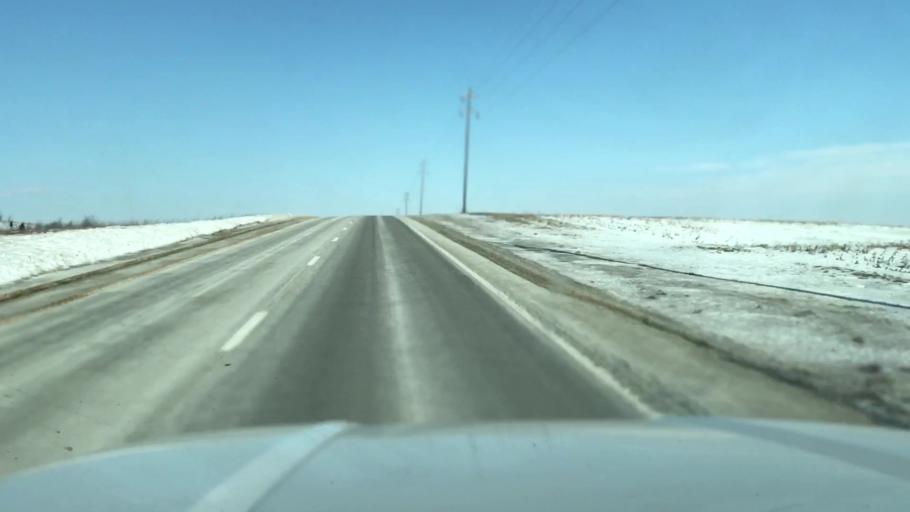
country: US
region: Missouri
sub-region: Andrew County
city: Savannah
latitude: 40.1213
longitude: -94.8696
